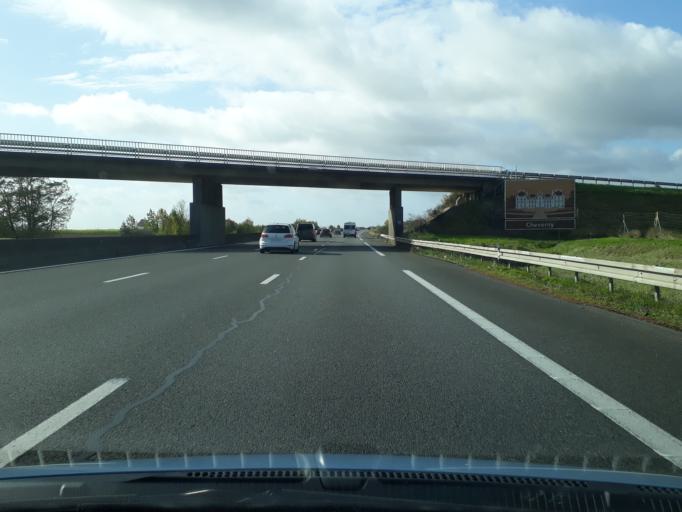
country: FR
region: Centre
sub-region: Departement du Loiret
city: Beaugency
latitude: 47.7868
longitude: 1.5996
